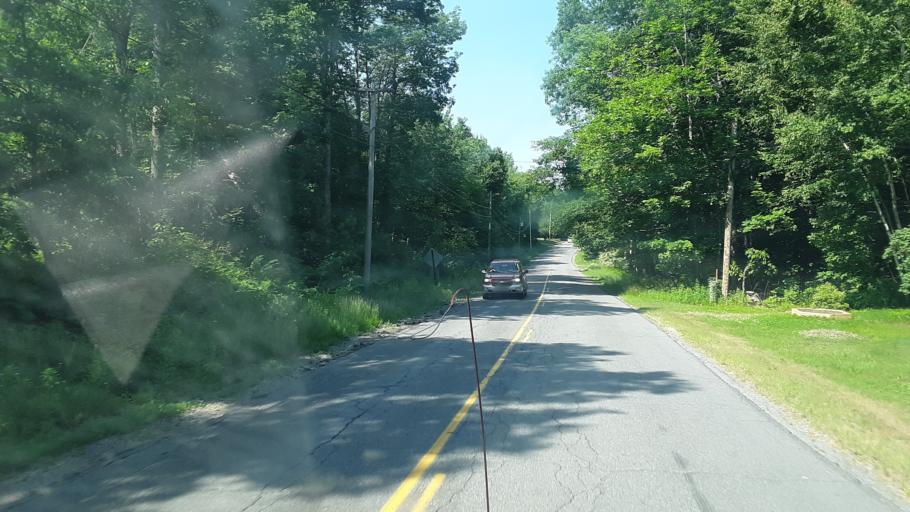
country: US
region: Maine
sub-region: Waldo County
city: Swanville
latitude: 44.5528
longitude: -68.9573
